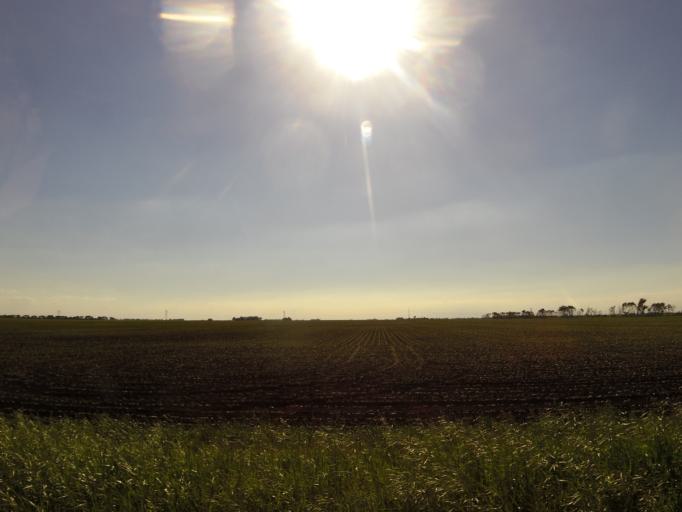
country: US
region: North Dakota
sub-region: Walsh County
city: Grafton
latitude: 48.4034
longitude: -97.2556
